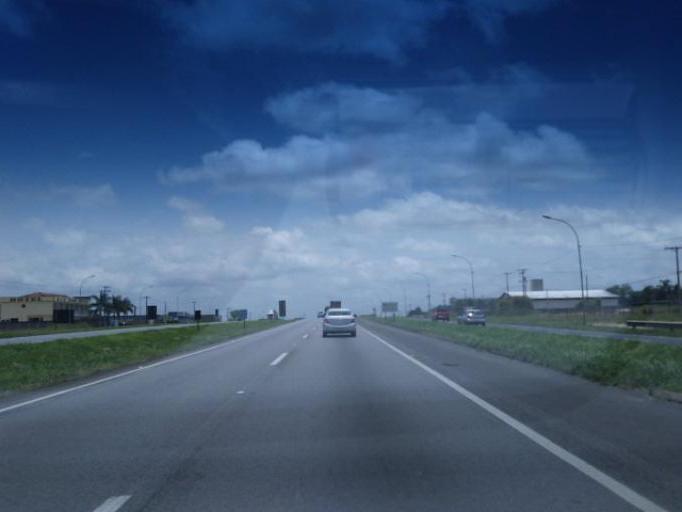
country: BR
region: Sao Paulo
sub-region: Registro
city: Registro
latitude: -24.5125
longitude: -47.8506
